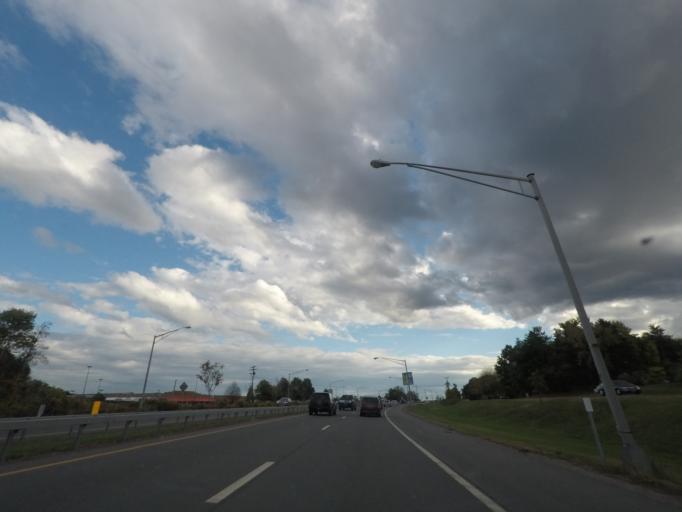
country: US
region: New York
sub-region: Albany County
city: McKownville
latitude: 42.6998
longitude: -73.8513
